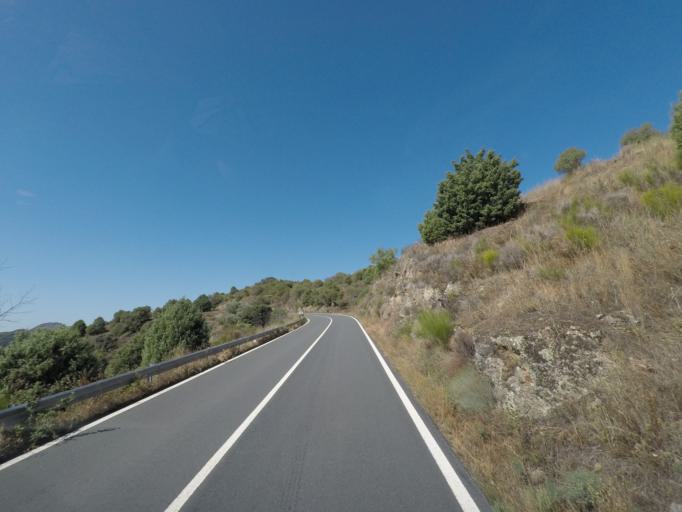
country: ES
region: Castille and Leon
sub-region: Provincia de Salamanca
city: Villarino de los Aires
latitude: 41.2993
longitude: -6.4790
